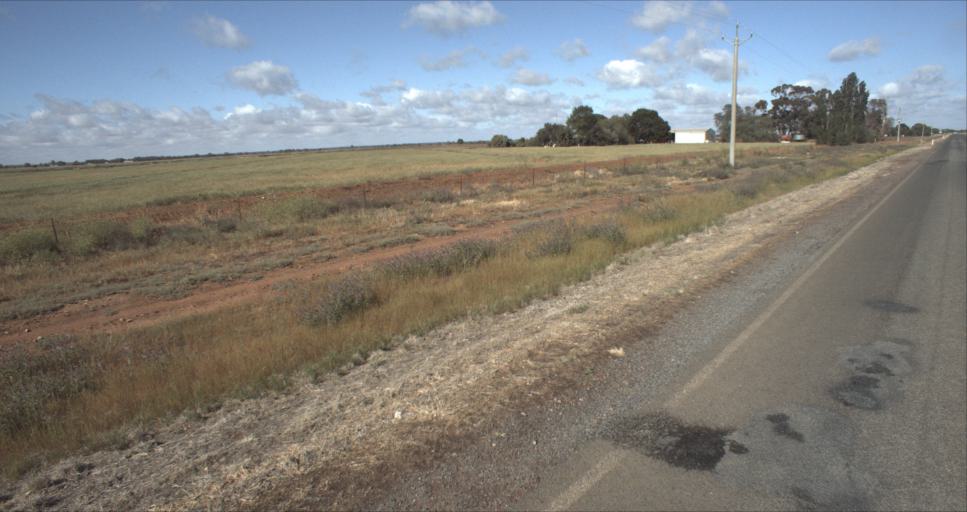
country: AU
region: New South Wales
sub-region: Leeton
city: Leeton
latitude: -34.5506
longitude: 146.3111
